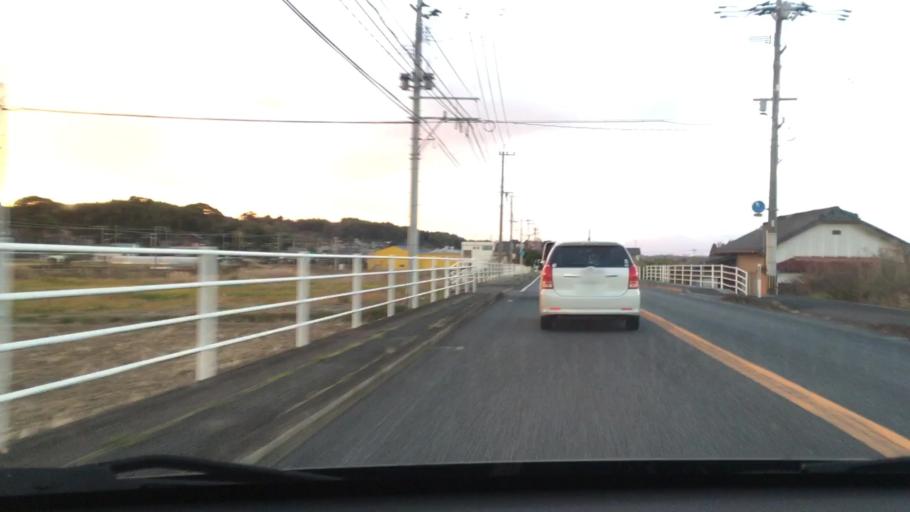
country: JP
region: Fukuoka
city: Shiida
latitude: 33.6309
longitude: 131.0831
